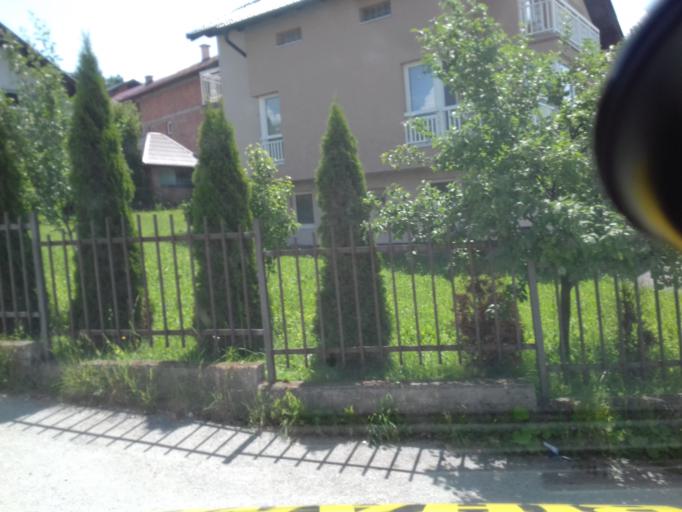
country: BA
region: Federation of Bosnia and Herzegovina
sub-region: Kanton Sarajevo
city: Sarajevo
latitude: 43.8623
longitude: 18.3222
